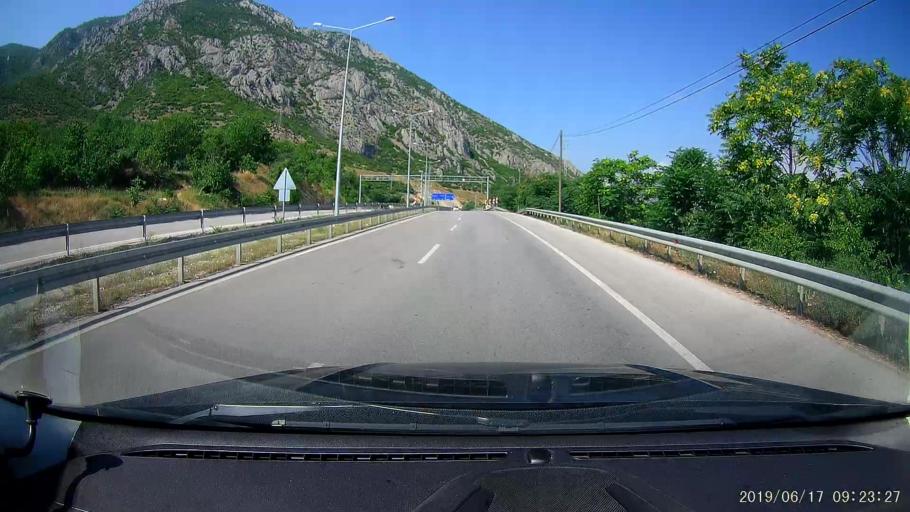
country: TR
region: Amasya
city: Amasya
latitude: 40.6758
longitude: 35.8734
